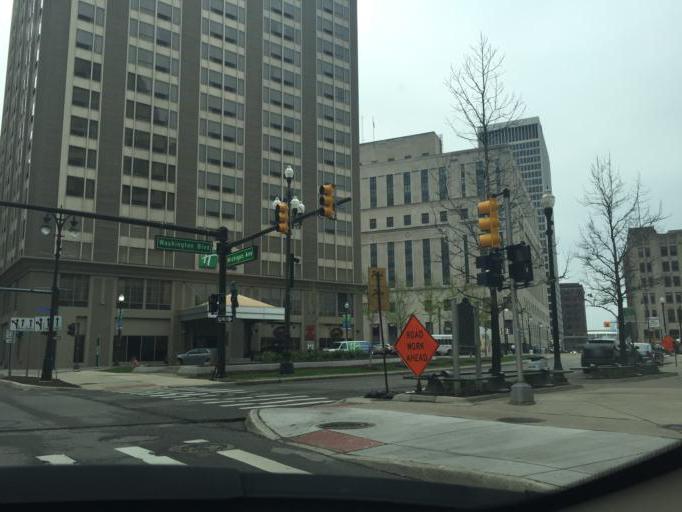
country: US
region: Michigan
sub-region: Wayne County
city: Detroit
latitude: 42.3316
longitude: -83.0515
